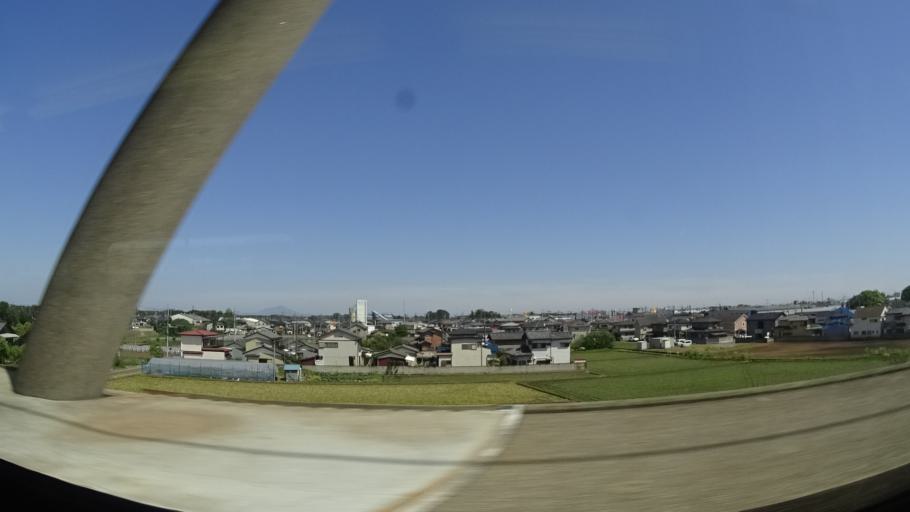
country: JP
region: Ibaraki
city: Koga
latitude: 36.2100
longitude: 139.7511
